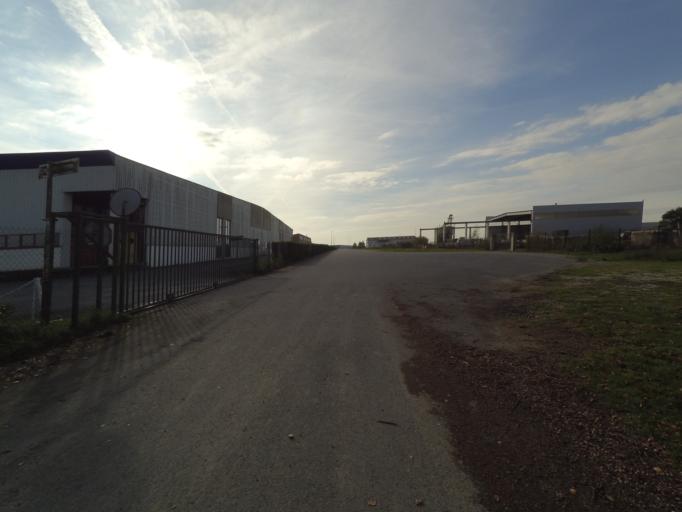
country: FR
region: Pays de la Loire
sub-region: Departement de la Vendee
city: Saint-Hilaire-de-Loulay
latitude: 47.0256
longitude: -1.3438
